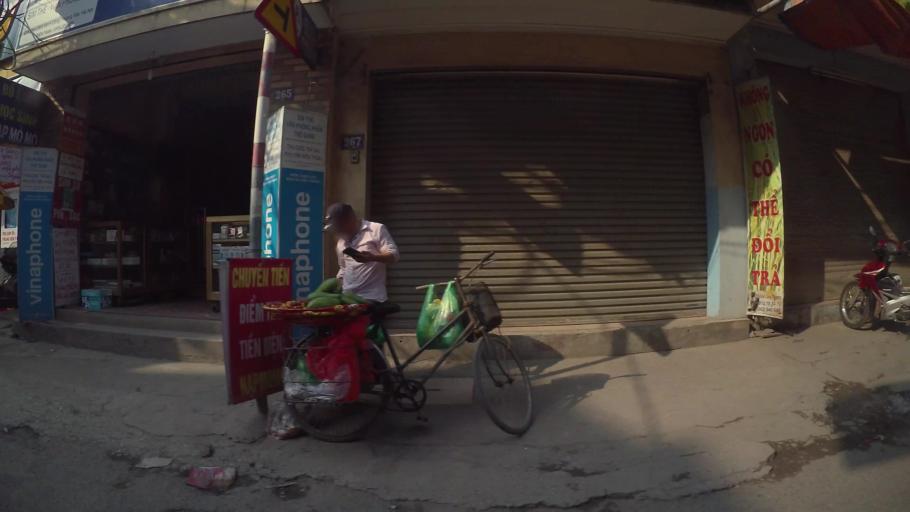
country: VN
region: Ha Noi
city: Thanh Xuan
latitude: 20.9844
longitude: 105.8236
